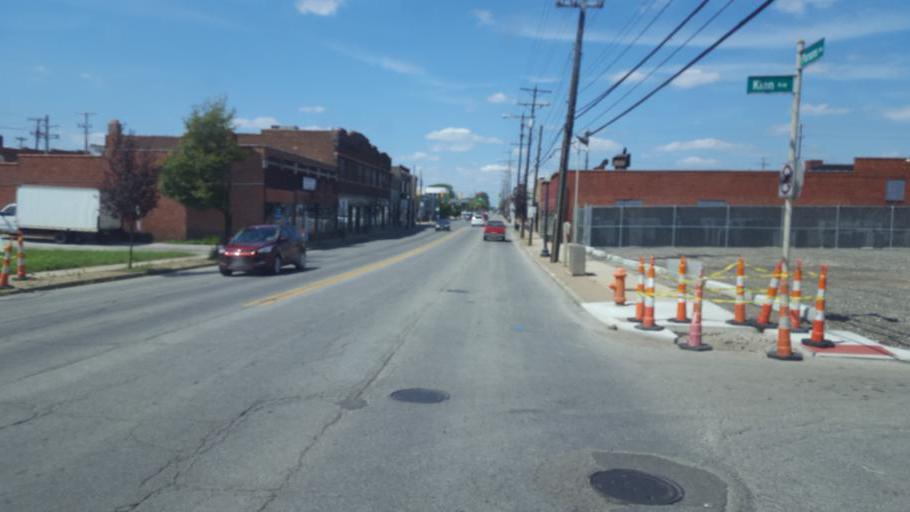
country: US
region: Ohio
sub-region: Franklin County
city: Columbus
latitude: 39.9227
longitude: -82.9845
